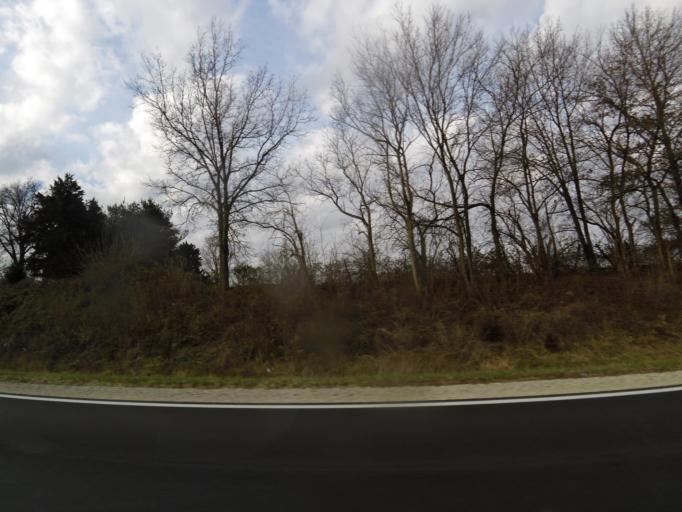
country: US
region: Illinois
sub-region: Christian County
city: Pana
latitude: 39.3537
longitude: -89.0818
